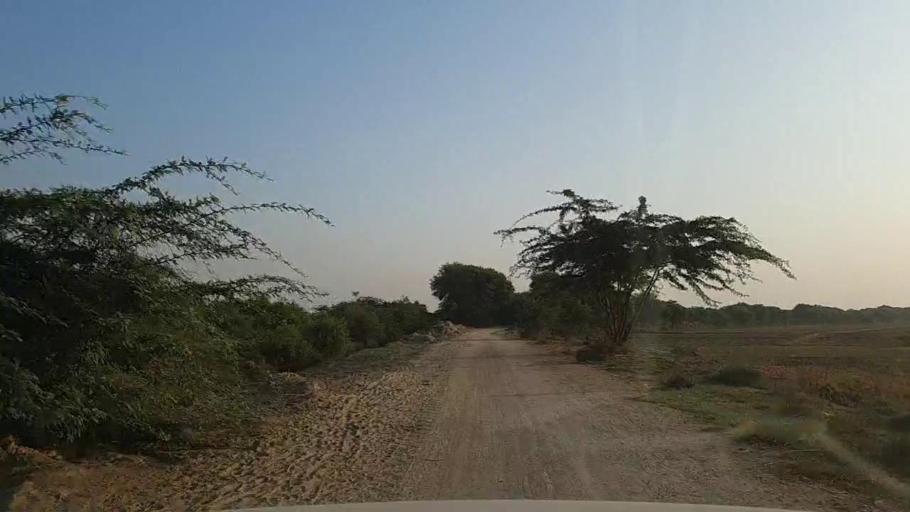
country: PK
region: Sindh
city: Daro Mehar
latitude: 24.7424
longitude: 68.1844
